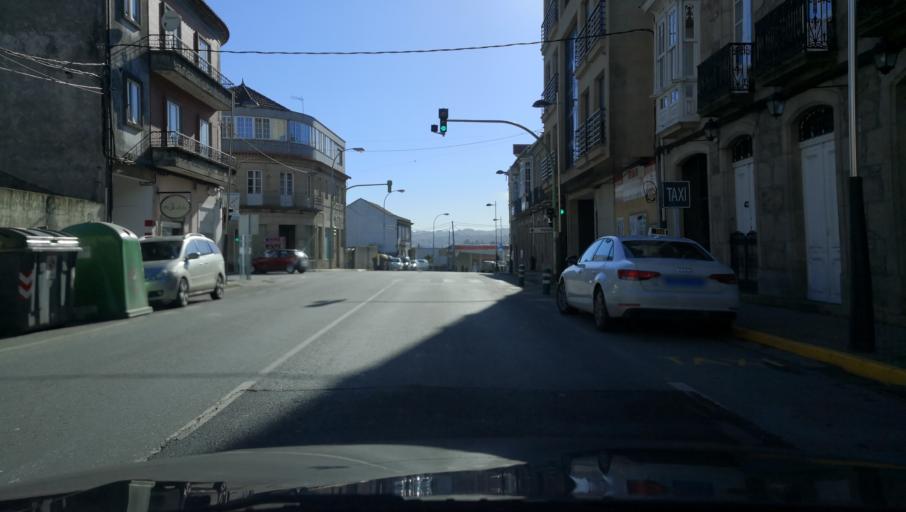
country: ES
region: Galicia
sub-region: Provincia de Pontevedra
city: Silleda
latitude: 42.7293
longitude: -8.3031
